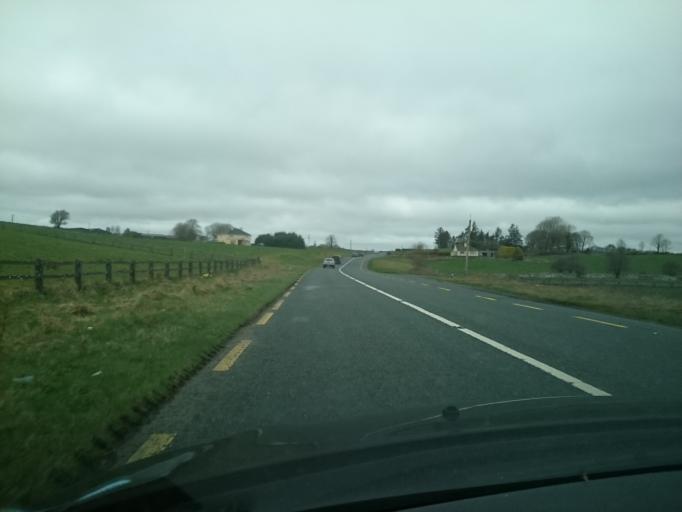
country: IE
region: Connaught
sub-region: Maigh Eo
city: Claremorris
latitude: 53.7820
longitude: -9.0794
